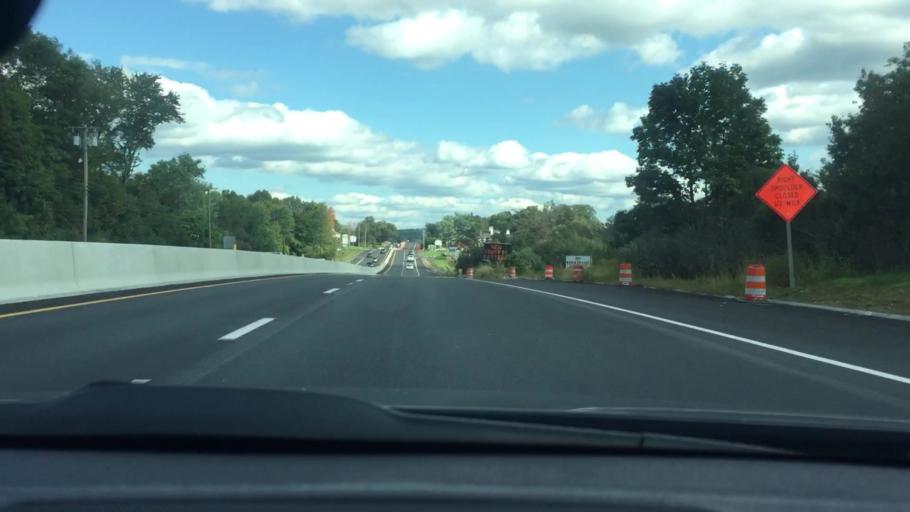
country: US
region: Massachusetts
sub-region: Worcester County
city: Westborough
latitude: 42.2838
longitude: -71.6299
